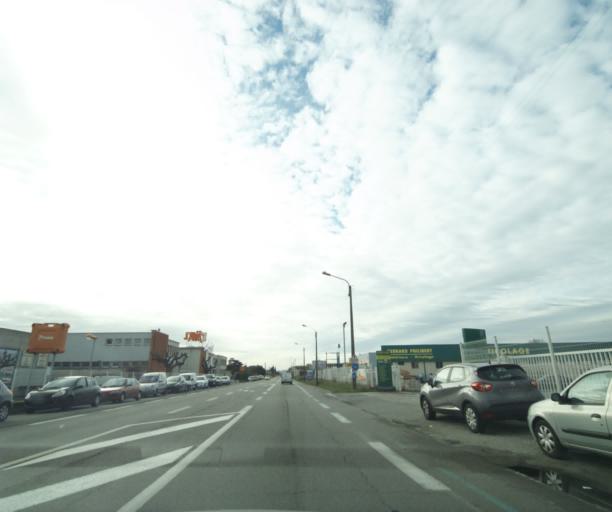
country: FR
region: Rhone-Alpes
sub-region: Departement de la Drome
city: Bourg-les-Valence
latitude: 44.9577
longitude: 4.8895
